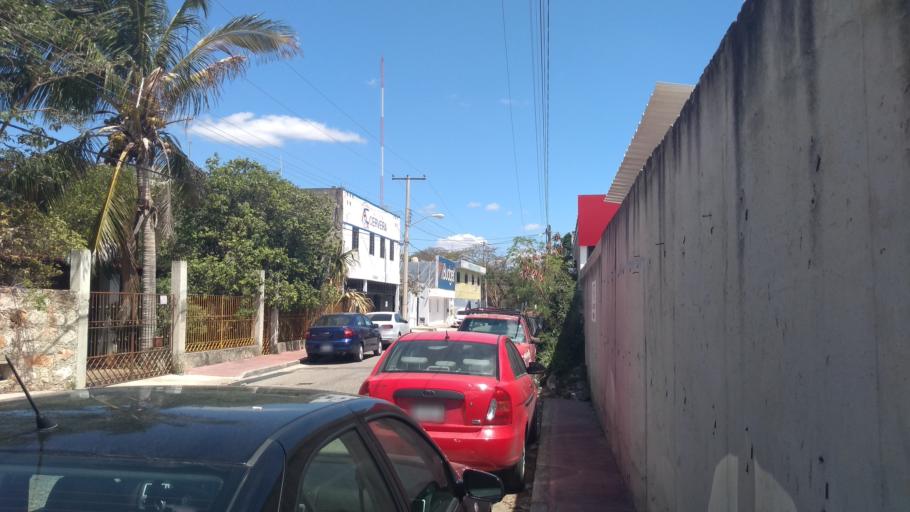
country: MX
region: Yucatan
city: Itzincab Palomeque
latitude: 20.9329
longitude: -89.6659
